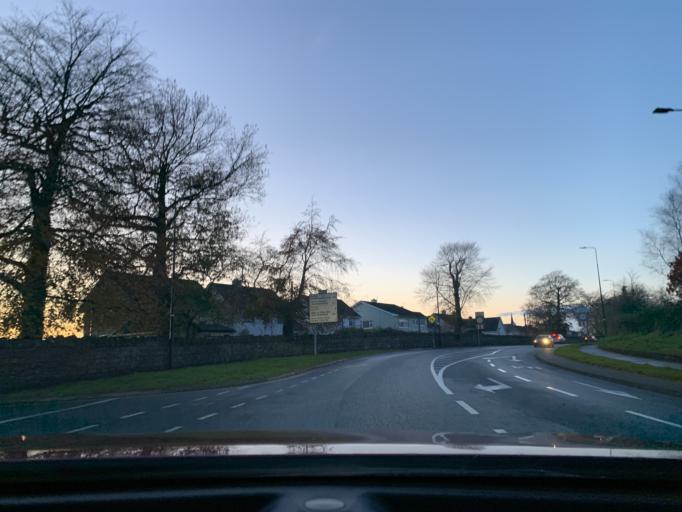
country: IE
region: Connaught
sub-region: County Leitrim
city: Carrick-on-Shannon
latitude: 53.9449
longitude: -8.0872
